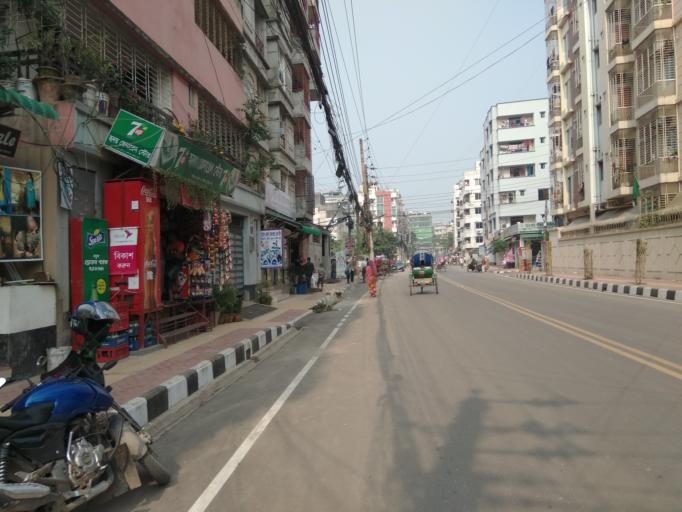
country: BD
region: Dhaka
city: Tungi
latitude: 23.8667
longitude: 90.3856
